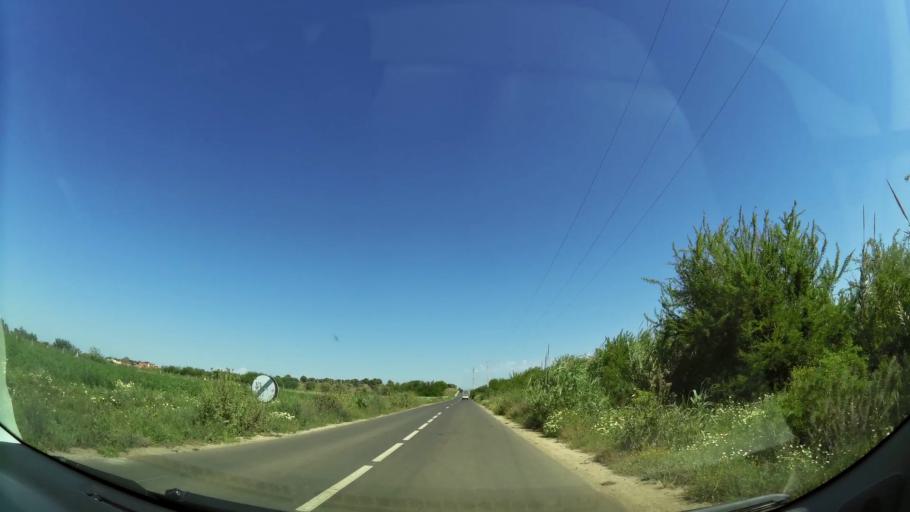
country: MA
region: Oriental
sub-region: Berkane-Taourirt
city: Madagh
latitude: 35.0156
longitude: -2.4040
